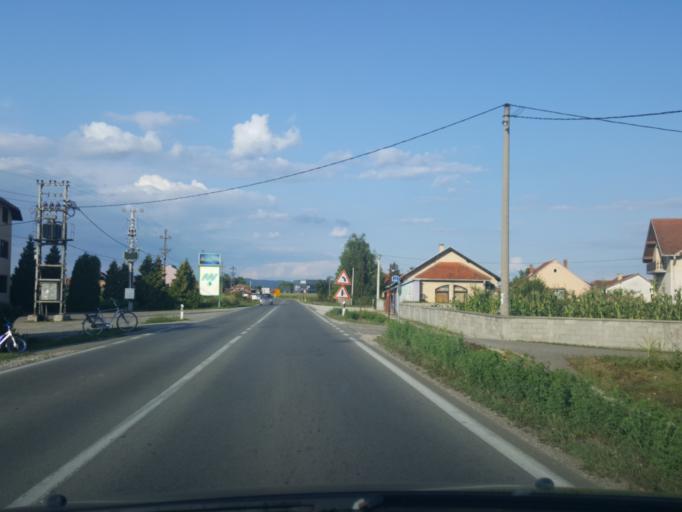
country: RS
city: Lipnicki Sor
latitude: 44.5790
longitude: 19.2499
